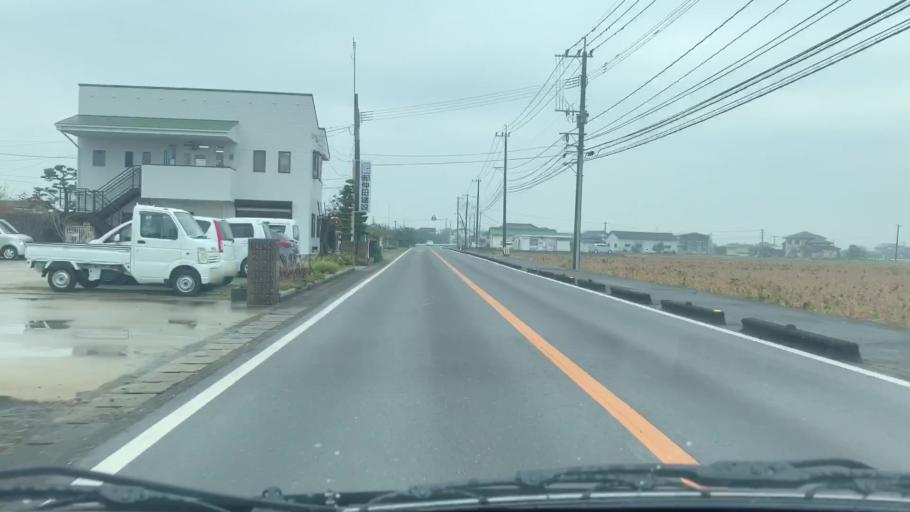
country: JP
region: Saga Prefecture
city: Takeocho-takeo
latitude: 33.1964
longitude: 130.1102
